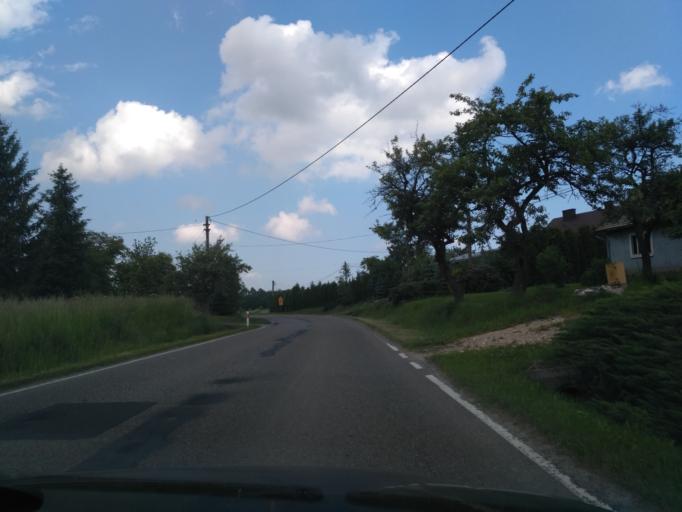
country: PL
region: Subcarpathian Voivodeship
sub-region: Powiat lancucki
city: Handzlowka
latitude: 49.9721
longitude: 22.1912
